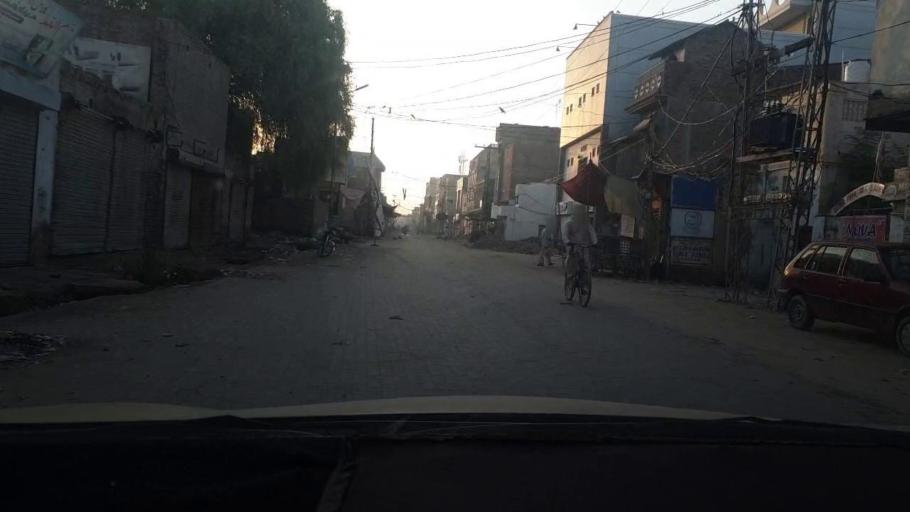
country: PK
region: Sindh
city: Larkana
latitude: 27.5507
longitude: 68.2164
